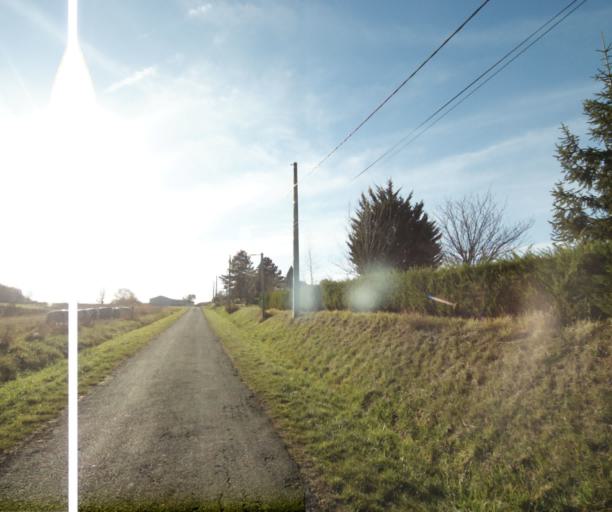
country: FR
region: Poitou-Charentes
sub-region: Departement de la Charente-Maritime
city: Burie
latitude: 45.7843
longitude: -0.4409
